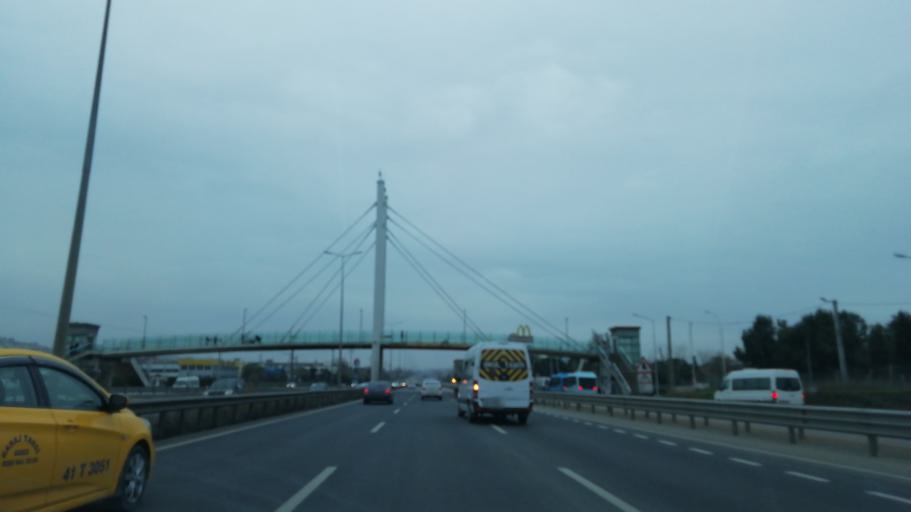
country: TR
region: Kocaeli
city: Darica
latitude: 40.8119
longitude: 29.3678
